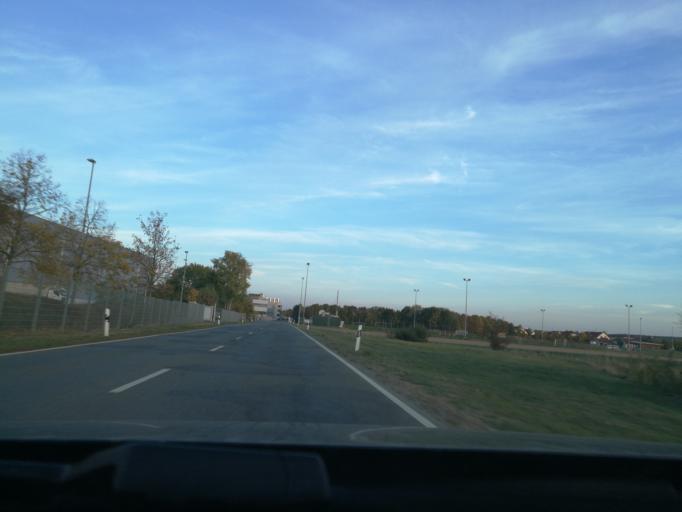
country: DE
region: Bavaria
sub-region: Regierungsbezirk Mittelfranken
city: Veitsbronn
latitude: 49.4963
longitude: 10.9060
